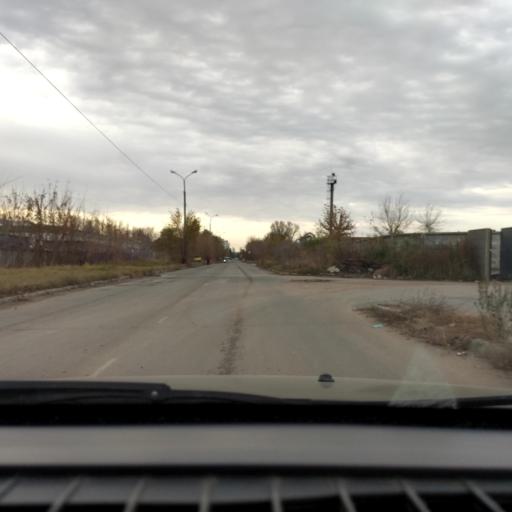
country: RU
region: Samara
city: Tol'yatti
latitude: 53.5570
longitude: 49.3145
